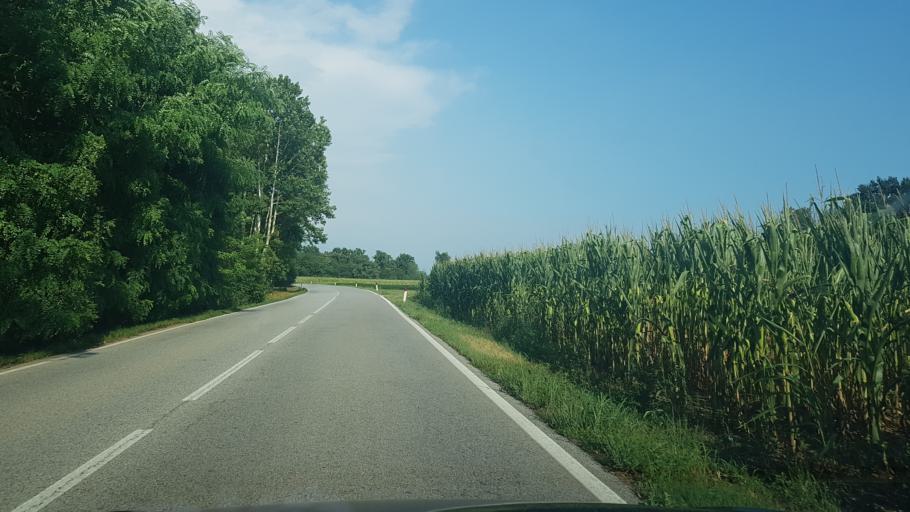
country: IT
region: Friuli Venezia Giulia
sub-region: Provincia di Udine
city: Basiliano-Vissandone
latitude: 46.0568
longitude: 13.1060
